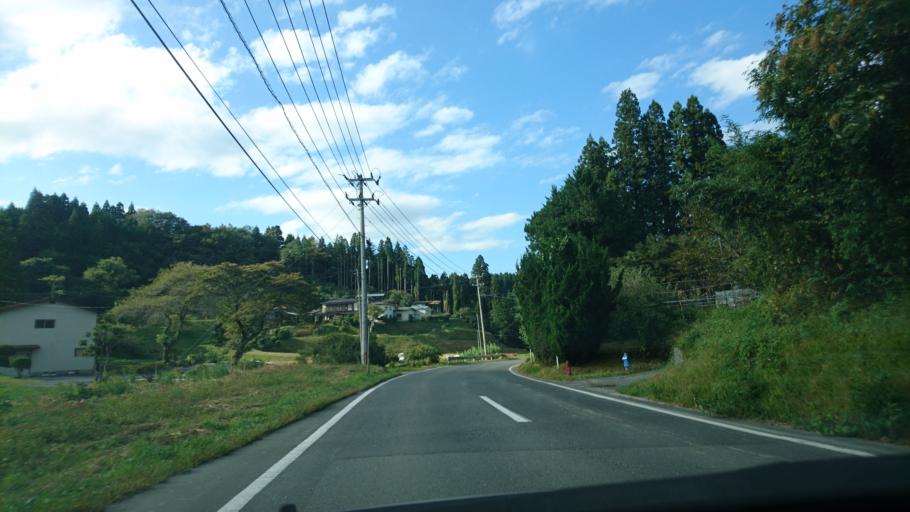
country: JP
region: Iwate
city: Ichinoseki
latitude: 38.8979
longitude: 141.3247
